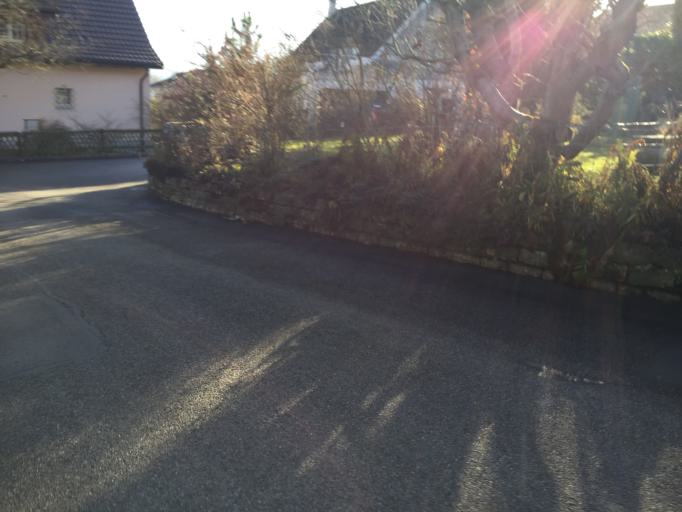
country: CH
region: Bern
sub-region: Bern-Mittelland District
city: Koniz
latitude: 46.9299
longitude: 7.4086
